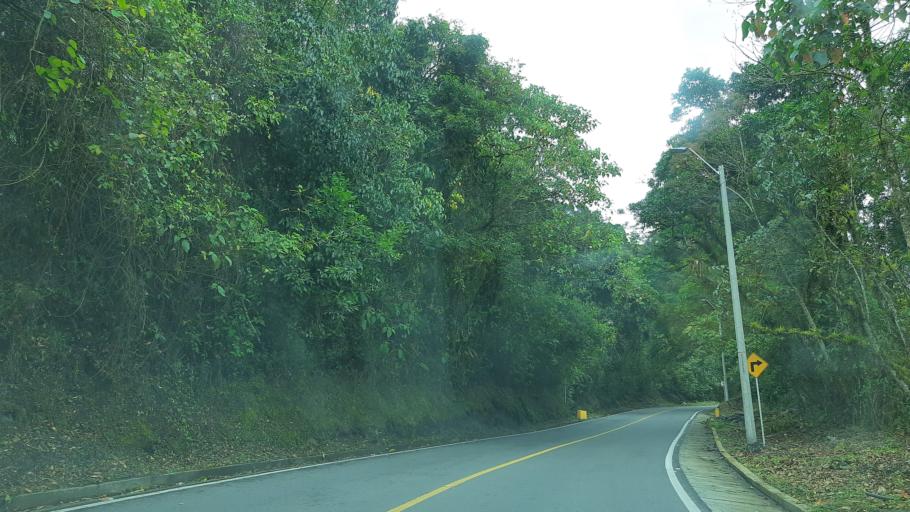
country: CO
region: Boyaca
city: Chivor
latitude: 4.9434
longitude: -73.3052
